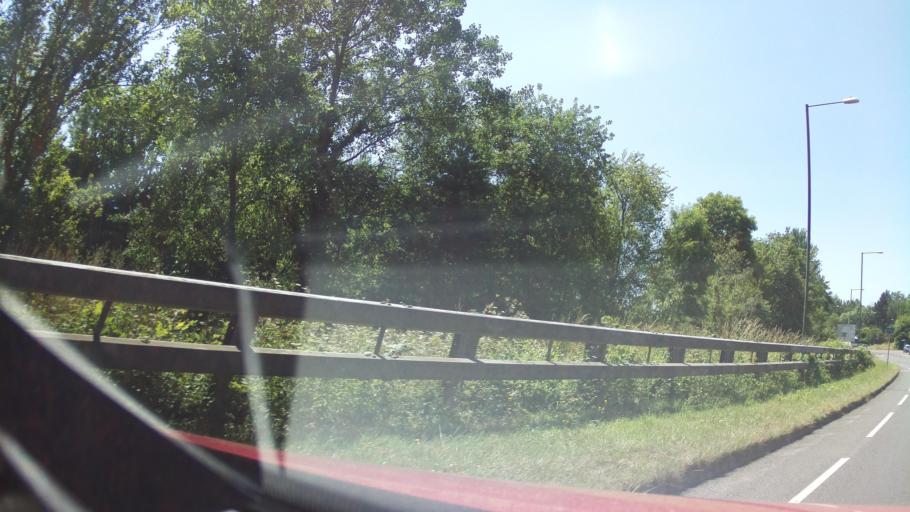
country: GB
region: England
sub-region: Devon
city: Kingskerswell
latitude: 50.4865
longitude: -3.5546
